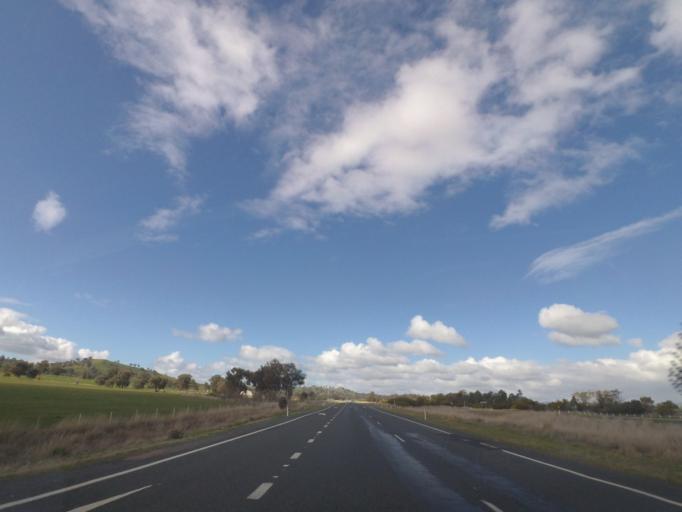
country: AU
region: New South Wales
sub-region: Greater Hume Shire
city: Jindera
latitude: -35.9252
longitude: 147.0663
